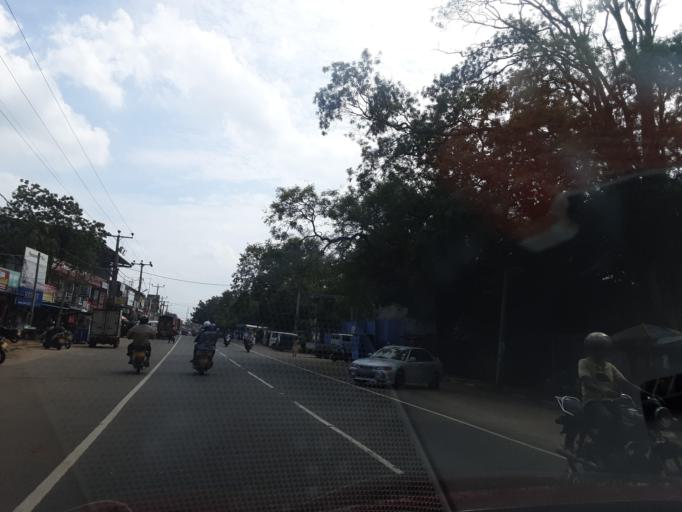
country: LK
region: Northern Province
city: Vavuniya
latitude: 8.5404
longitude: 80.4923
